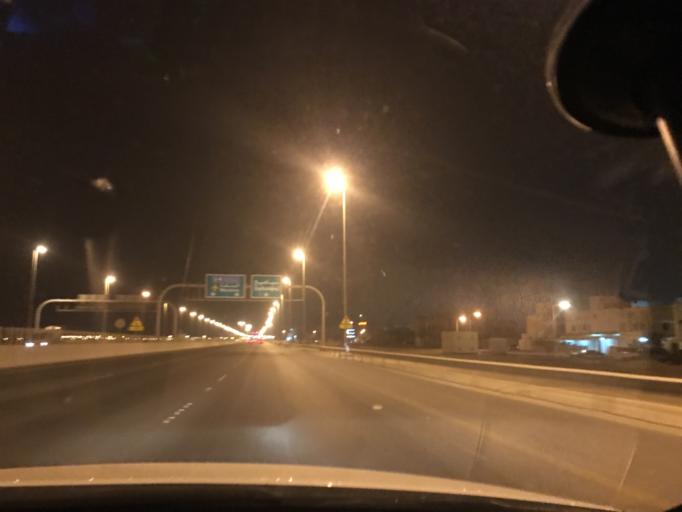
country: BH
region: Muharraq
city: Al Muharraq
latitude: 26.2863
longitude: 50.6399
